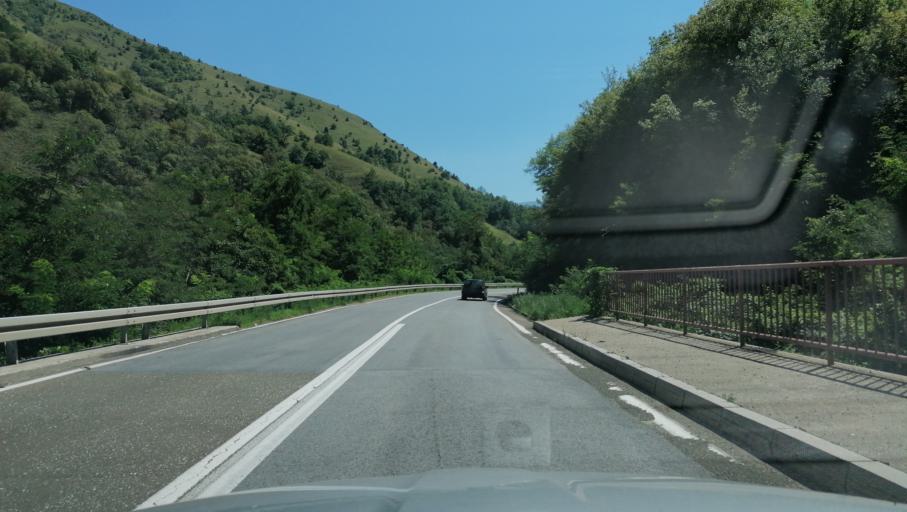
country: RS
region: Central Serbia
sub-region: Raski Okrug
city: Kraljevo
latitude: 43.5745
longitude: 20.5914
